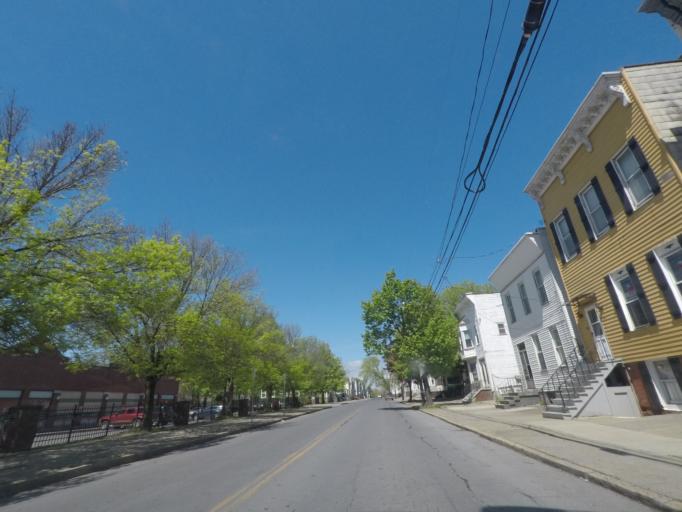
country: US
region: New York
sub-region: Albany County
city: Albany
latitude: 42.6639
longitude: -73.7589
